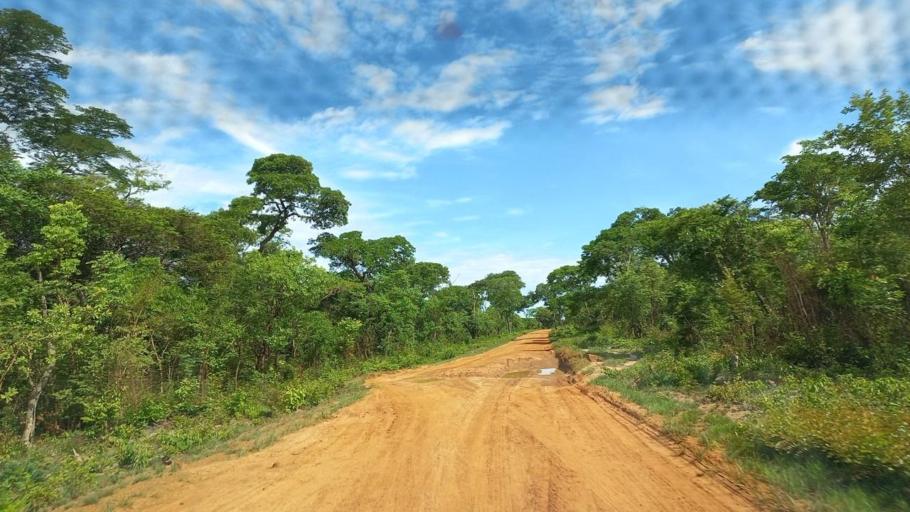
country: ZM
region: North-Western
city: Kabompo
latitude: -13.0768
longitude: 24.2188
